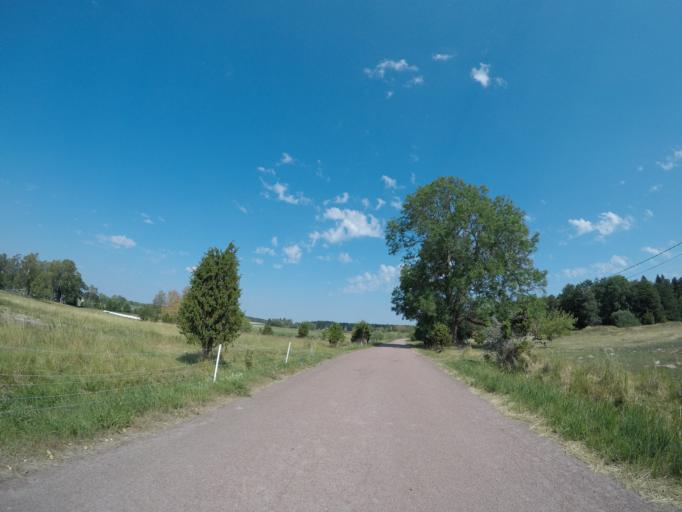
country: AX
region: Alands landsbygd
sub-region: Finstroem
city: Finstroem
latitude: 60.2067
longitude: 19.9018
